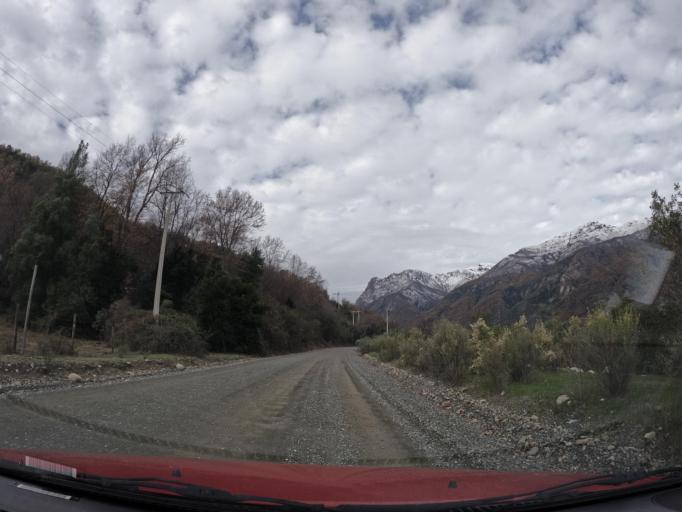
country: CL
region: Maule
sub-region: Provincia de Linares
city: Colbun
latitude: -35.8585
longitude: -71.2422
